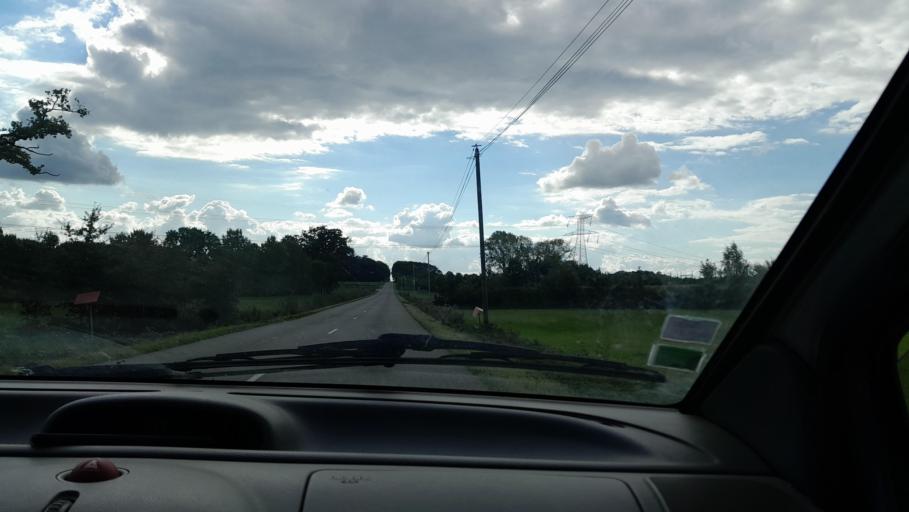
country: FR
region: Brittany
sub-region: Departement d'Ille-et-Vilaine
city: Le Pertre
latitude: 47.9867
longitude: -0.9987
